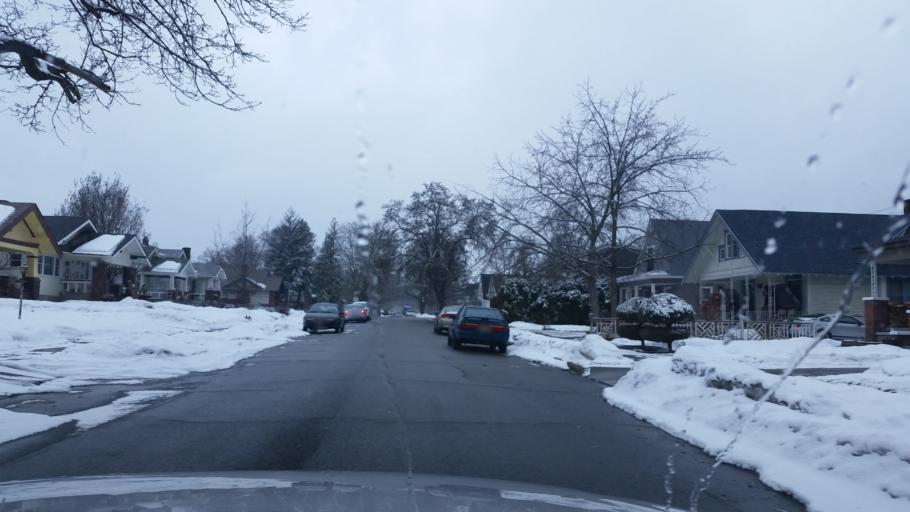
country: US
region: Washington
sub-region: Spokane County
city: Spokane
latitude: 47.6777
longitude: -117.4223
